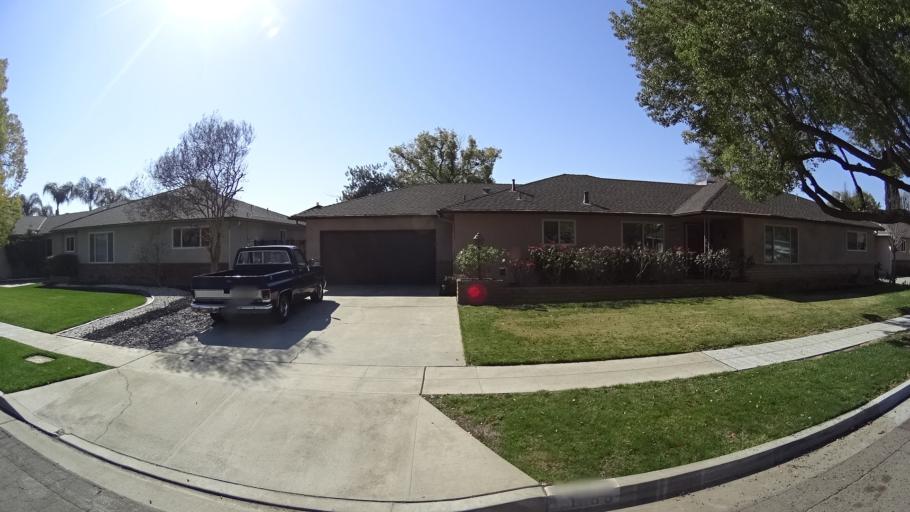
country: US
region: California
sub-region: Fresno County
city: Clovis
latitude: 36.8275
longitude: -119.7567
